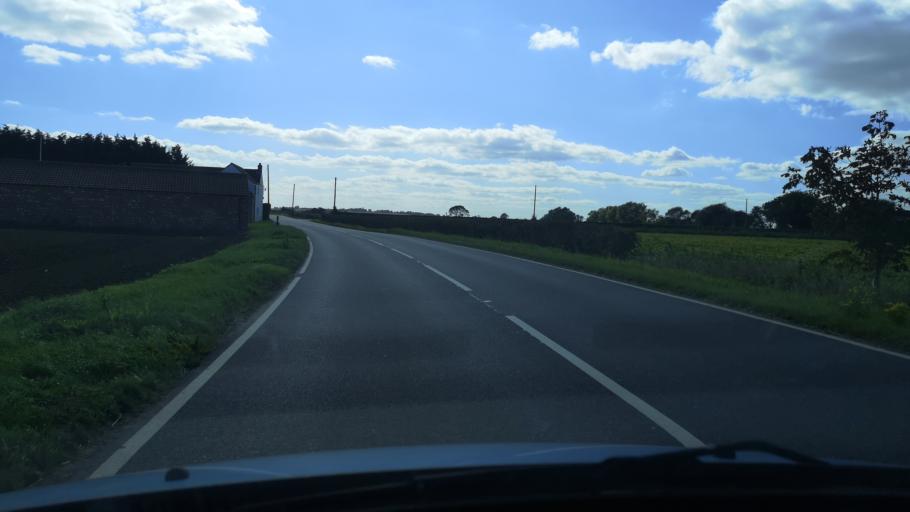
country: GB
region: England
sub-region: North Lincolnshire
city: Eastoft
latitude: 53.6299
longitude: -0.7974
